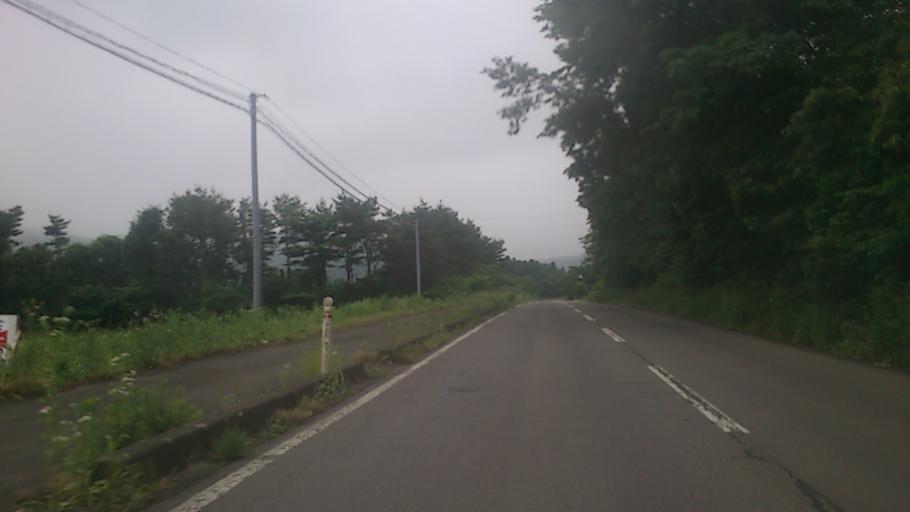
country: JP
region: Miyagi
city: Shiroishi
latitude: 38.1080
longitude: 140.5648
